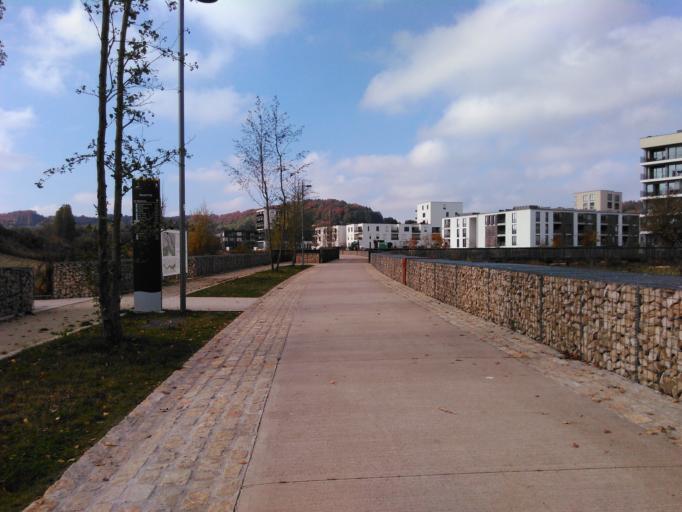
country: LU
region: Luxembourg
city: Belvaux
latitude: 49.5071
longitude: 5.9382
